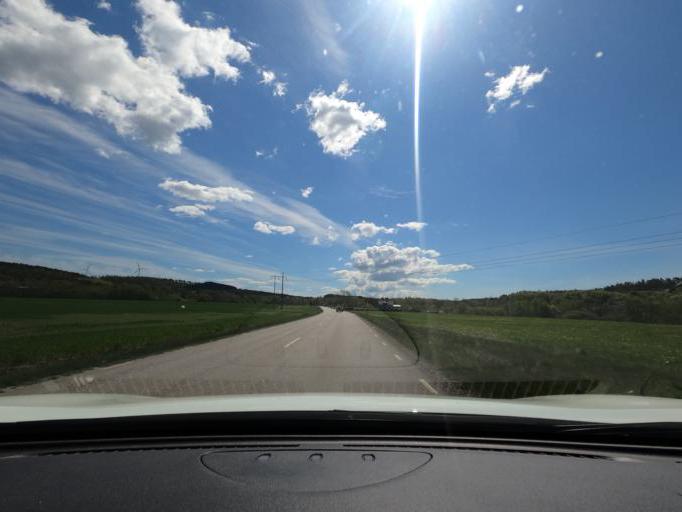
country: SE
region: Halland
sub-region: Kungsbacka Kommun
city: Fjaeras kyrkby
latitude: 57.4225
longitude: 12.1996
